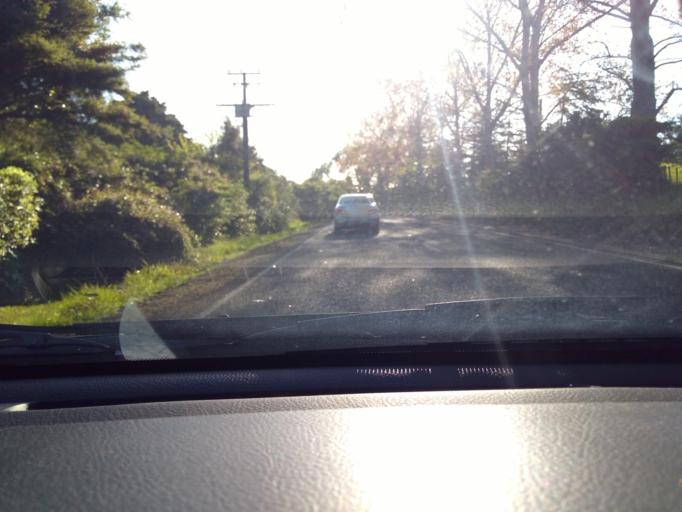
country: NZ
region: Auckland
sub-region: Auckland
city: Warkworth
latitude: -36.3933
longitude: 174.6665
